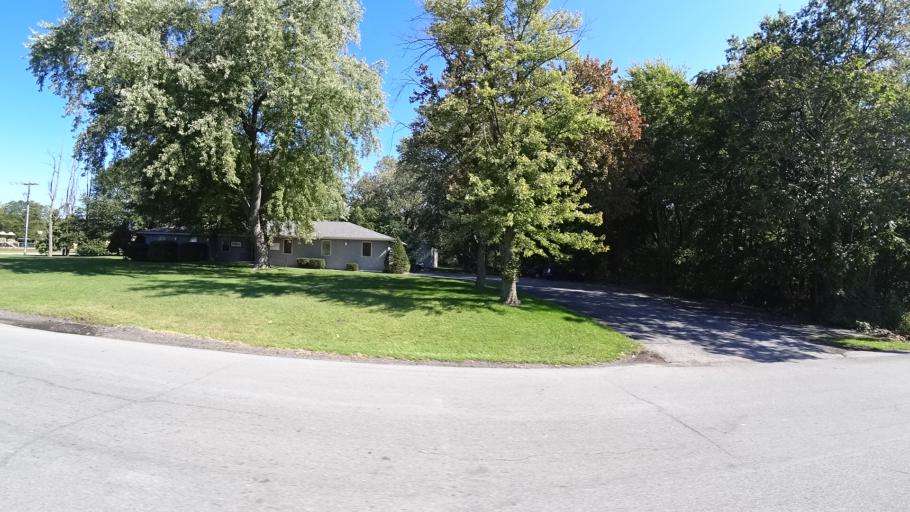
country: US
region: Indiana
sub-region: LaPorte County
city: Trail Creek
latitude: 41.6940
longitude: -86.8744
